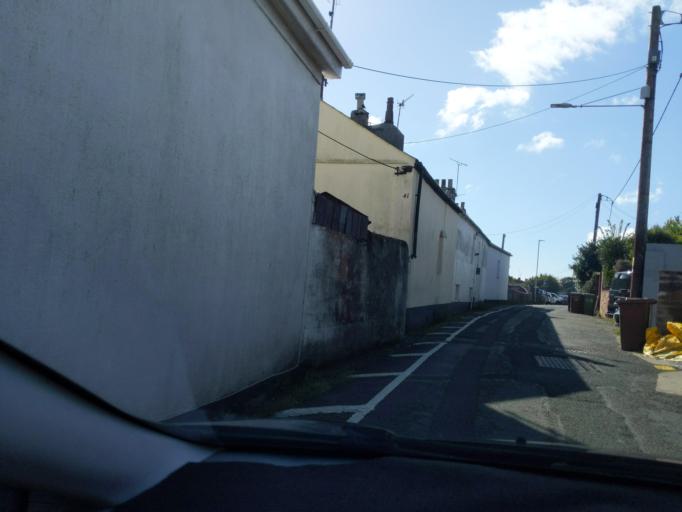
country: GB
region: England
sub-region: Plymouth
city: Plymstock
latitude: 50.3577
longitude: -4.0685
